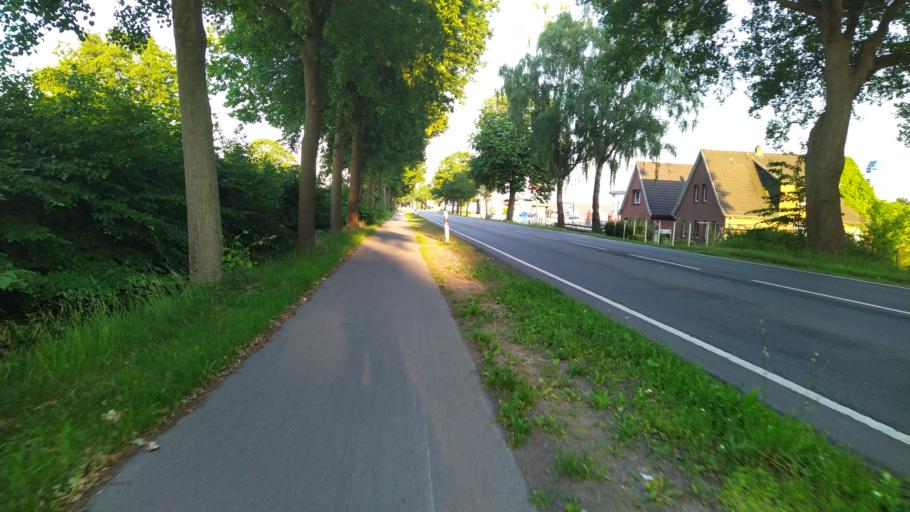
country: DE
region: Lower Saxony
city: Bei der Hohne
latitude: 53.4953
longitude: 9.1150
